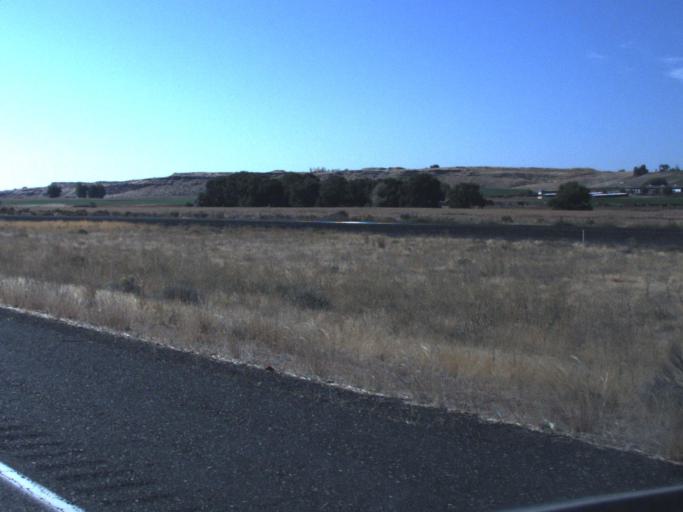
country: US
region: Washington
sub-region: Franklin County
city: Basin City
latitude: 46.4871
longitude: -119.0124
